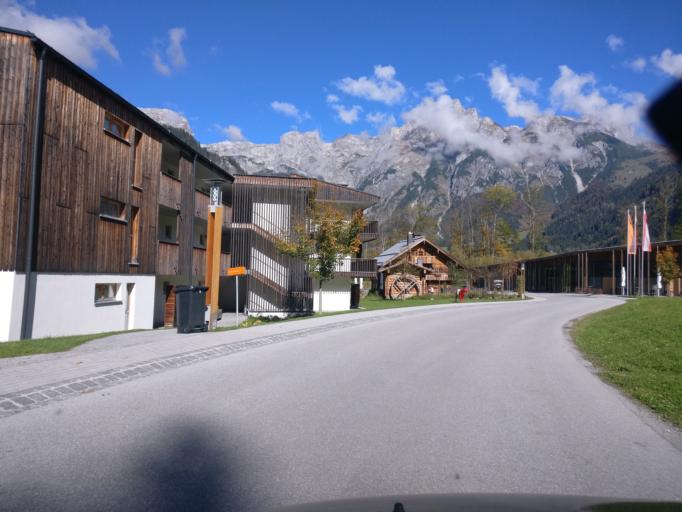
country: AT
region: Salzburg
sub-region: Politischer Bezirk Sankt Johann im Pongau
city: Werfenweng
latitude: 47.4616
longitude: 13.2602
